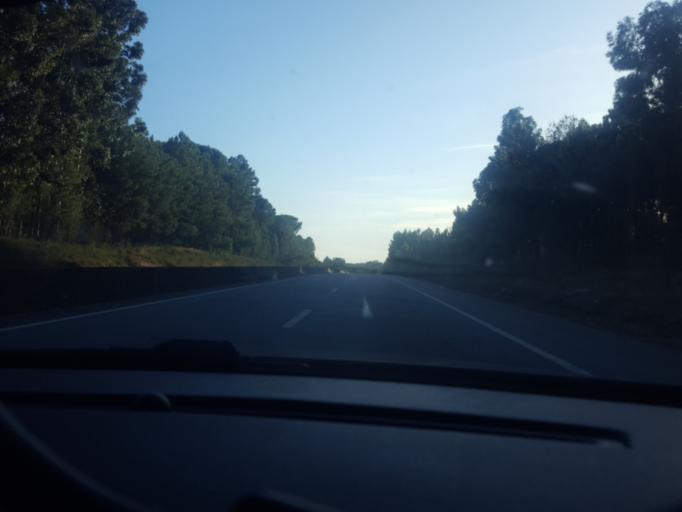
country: PT
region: Viseu
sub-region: Concelho de Carregal do Sal
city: Carregal do Sal
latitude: 40.4669
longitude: -7.9419
